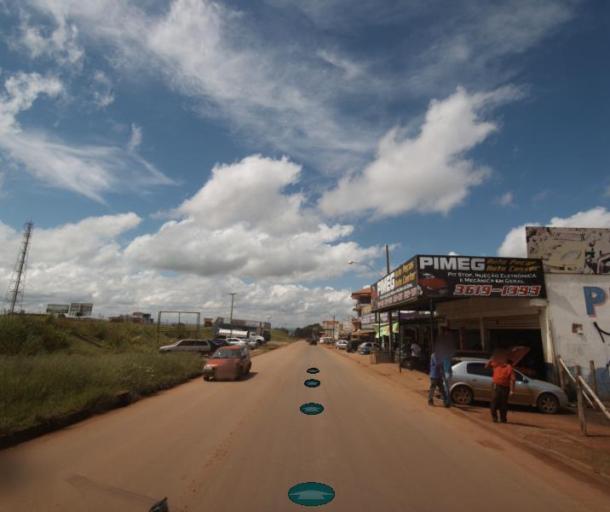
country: BR
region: Federal District
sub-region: Brasilia
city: Brasilia
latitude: -15.7532
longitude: -48.2592
